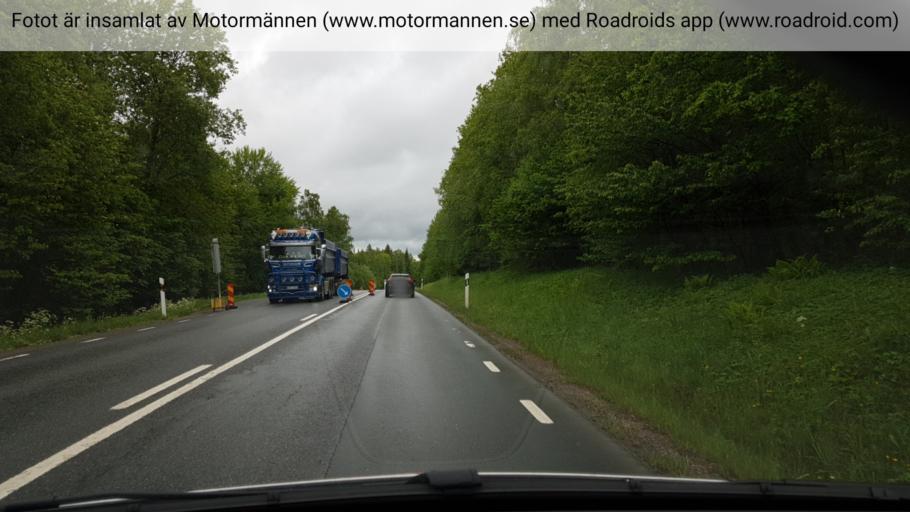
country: SE
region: Joenkoeping
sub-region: Aneby Kommun
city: Aneby
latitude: 57.9100
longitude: 14.8987
